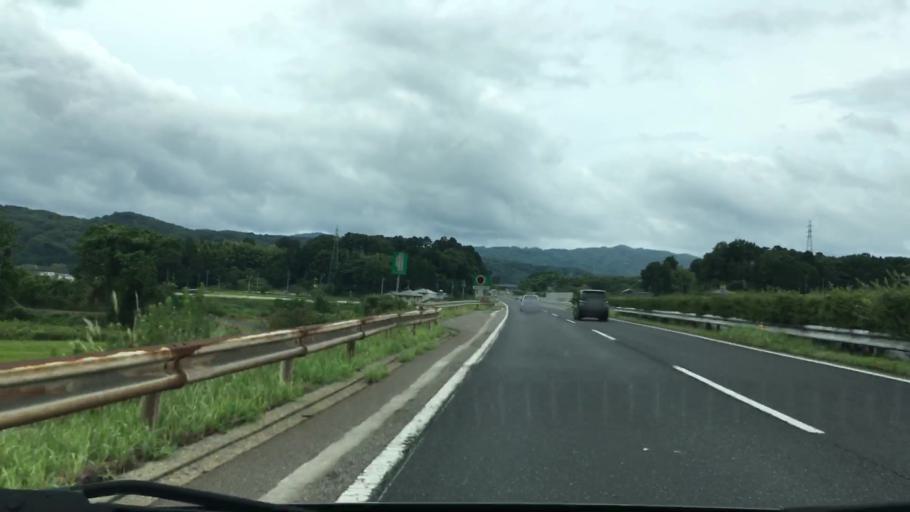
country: JP
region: Okayama
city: Tsuyama
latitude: 35.0621
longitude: 133.9360
